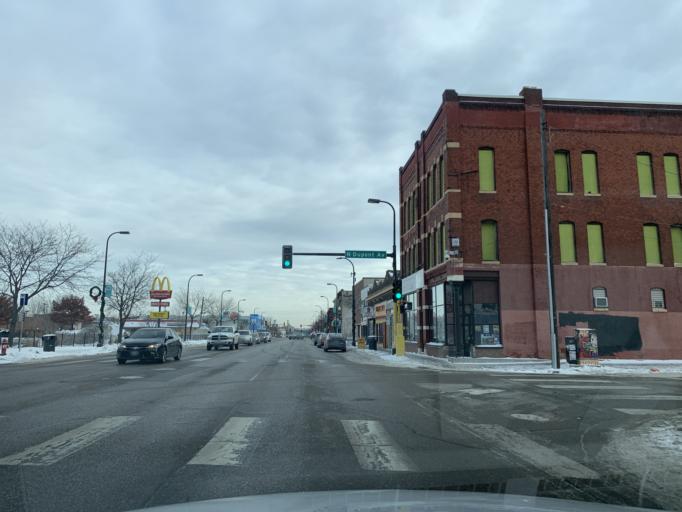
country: US
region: Minnesota
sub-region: Hennepin County
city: Minneapolis
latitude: 44.9991
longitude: -93.2930
